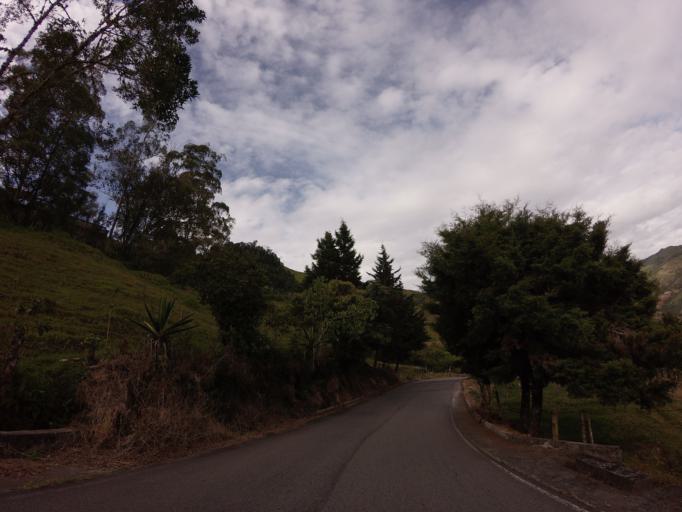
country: CO
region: Tolima
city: Casabianca
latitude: 5.1408
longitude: -75.1291
